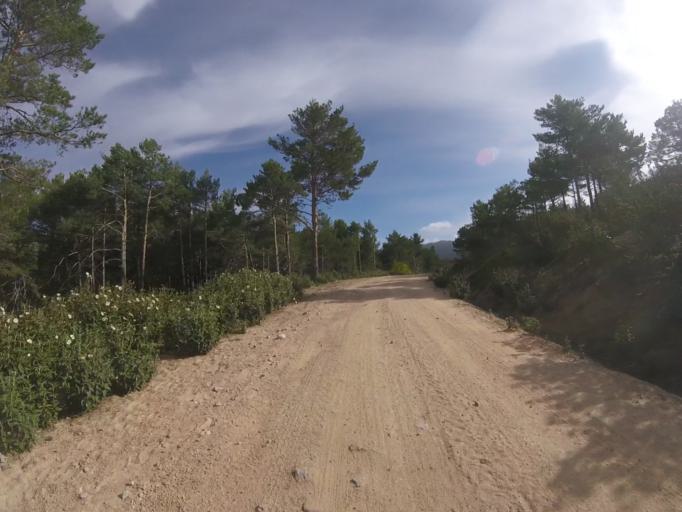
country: ES
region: Castille and Leon
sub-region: Provincia de Avila
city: Peguerinos
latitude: 40.6573
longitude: -4.1856
